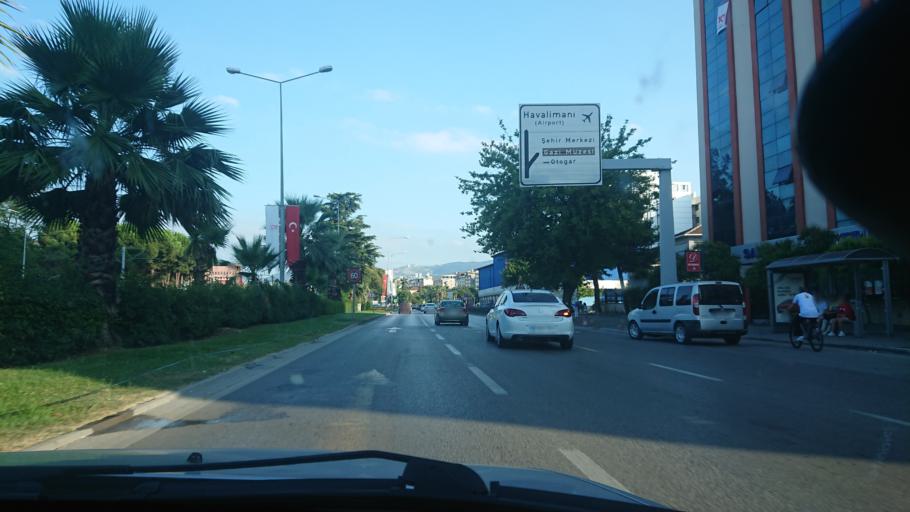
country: TR
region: Samsun
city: Samsun
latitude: 41.2923
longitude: 36.3349
